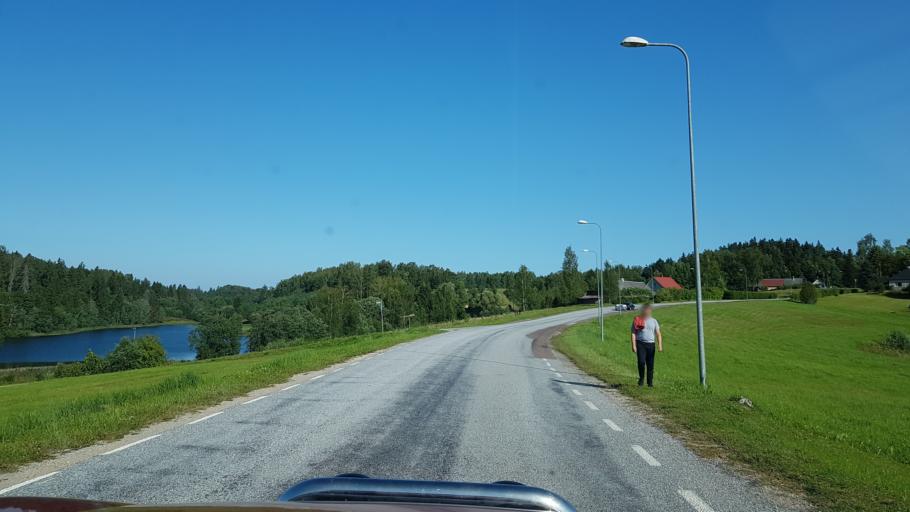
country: EE
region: Vorumaa
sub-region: Voru linn
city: Voru
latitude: 57.7310
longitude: 26.9161
